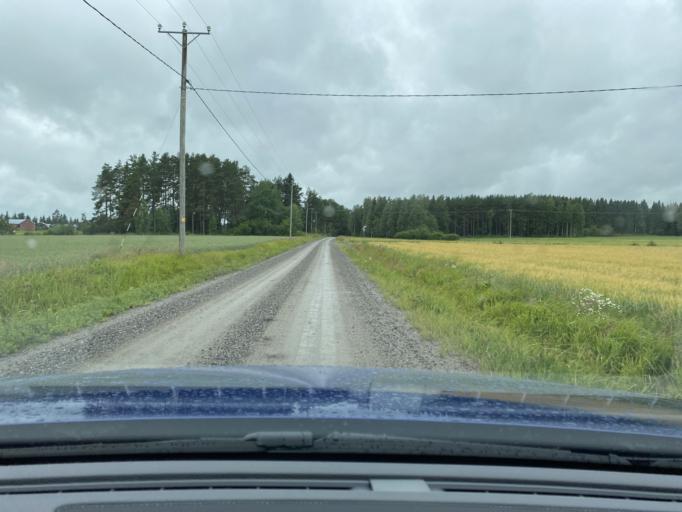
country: FI
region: Pirkanmaa
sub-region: Lounais-Pirkanmaa
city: Punkalaidun
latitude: 61.1469
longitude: 23.2812
